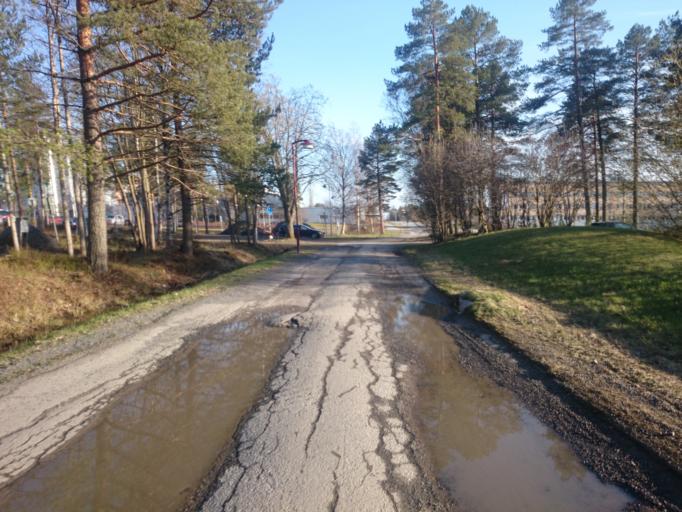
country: SE
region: Vaesterbotten
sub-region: Umea Kommun
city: Umea
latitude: 63.8191
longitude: 20.3151
